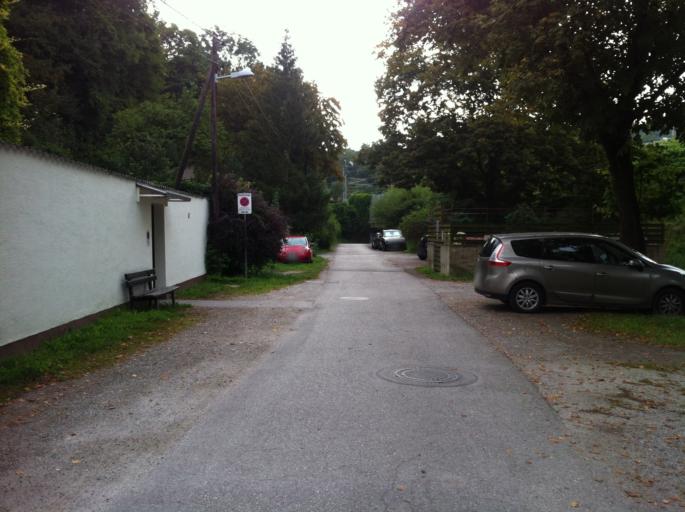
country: AT
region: Lower Austria
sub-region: Politischer Bezirk Wien-Umgebung
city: Purkersdorf
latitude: 48.2067
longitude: 16.2003
